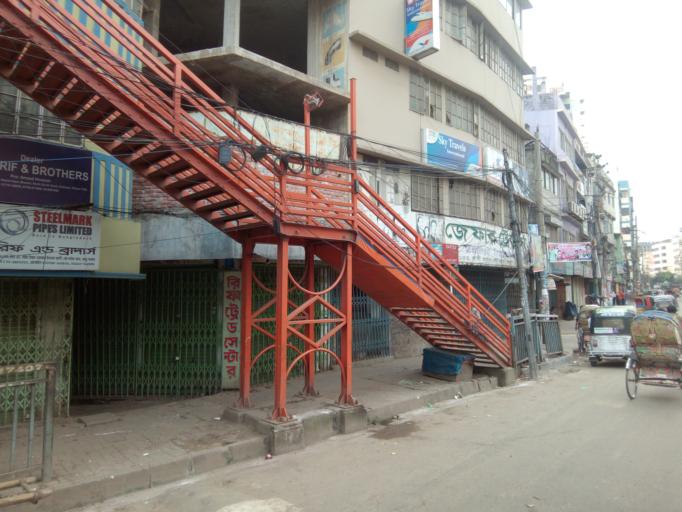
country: BD
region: Dhaka
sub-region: Dhaka
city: Dhaka
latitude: 23.7198
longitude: 90.4096
